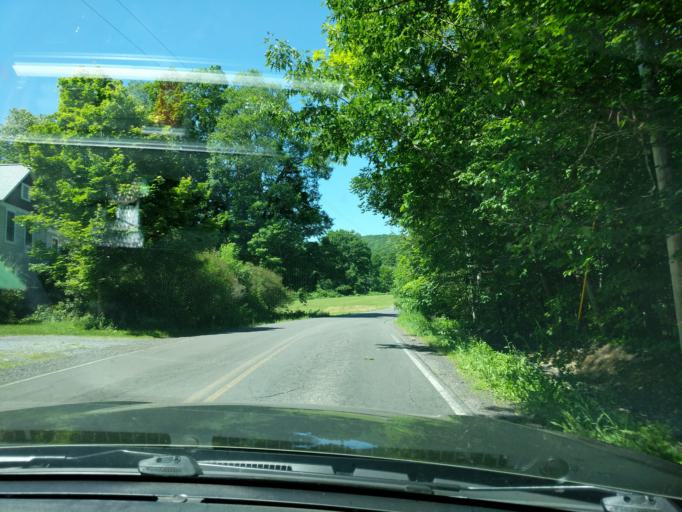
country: US
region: New York
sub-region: Tompkins County
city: East Ithaca
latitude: 42.3686
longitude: -76.4091
